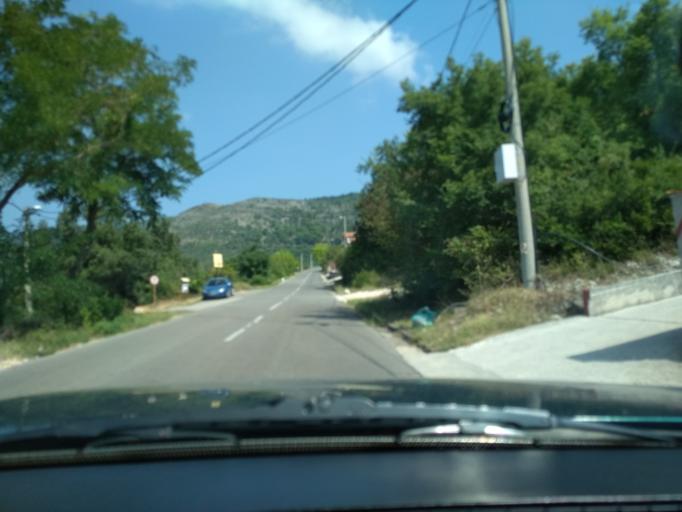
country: ME
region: Kotor
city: Kotor
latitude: 42.3953
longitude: 18.7550
